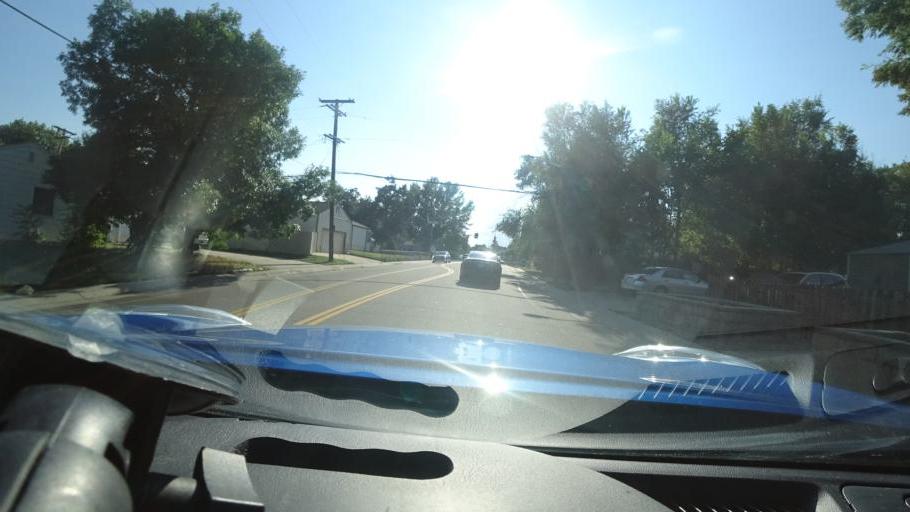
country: US
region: Colorado
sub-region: Arapahoe County
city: Sheridan
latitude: 39.6783
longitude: -105.0289
